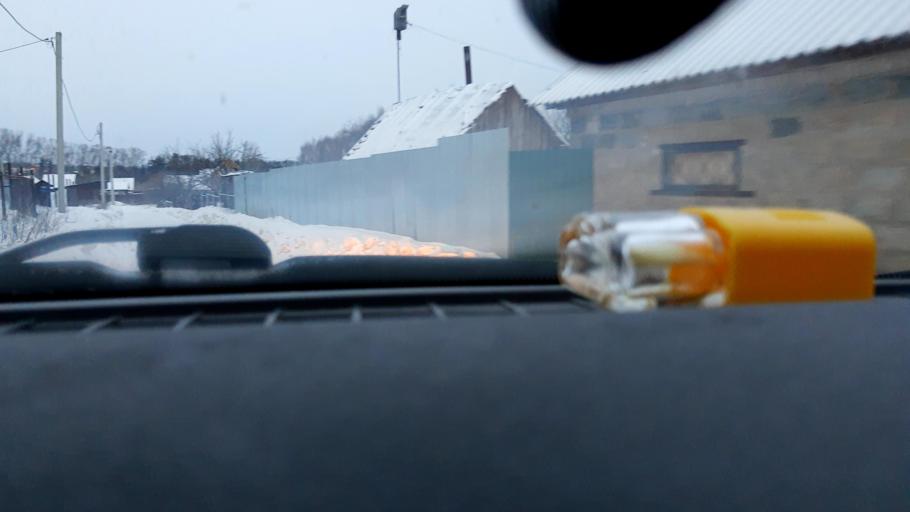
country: RU
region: Bashkortostan
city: Iglino
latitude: 54.8010
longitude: 56.4279
